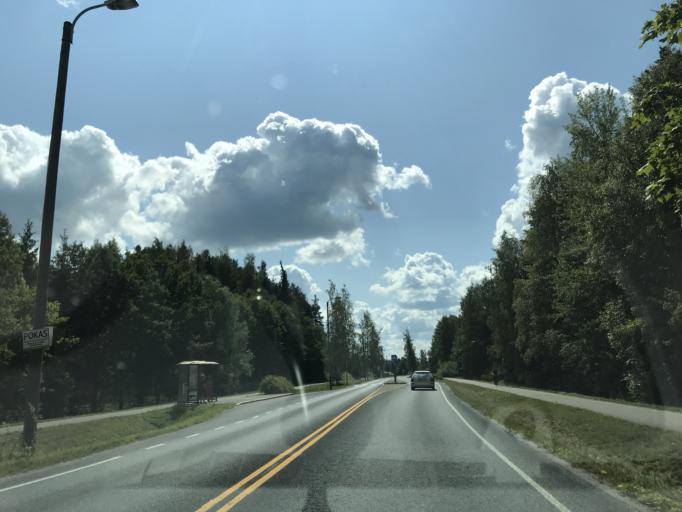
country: FI
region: Paijanne Tavastia
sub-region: Lahti
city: Orimattila
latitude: 60.8168
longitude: 25.7303
